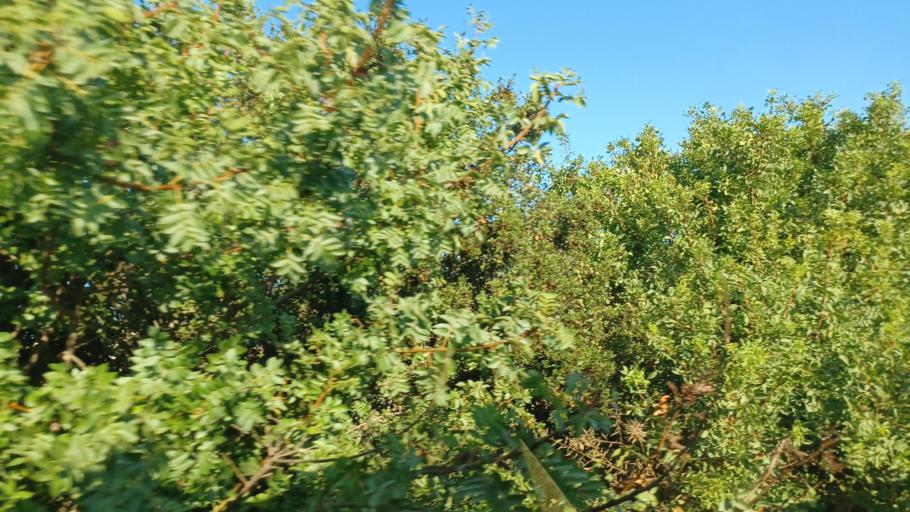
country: CY
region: Pafos
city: Mesogi
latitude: 34.8624
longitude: 32.5130
